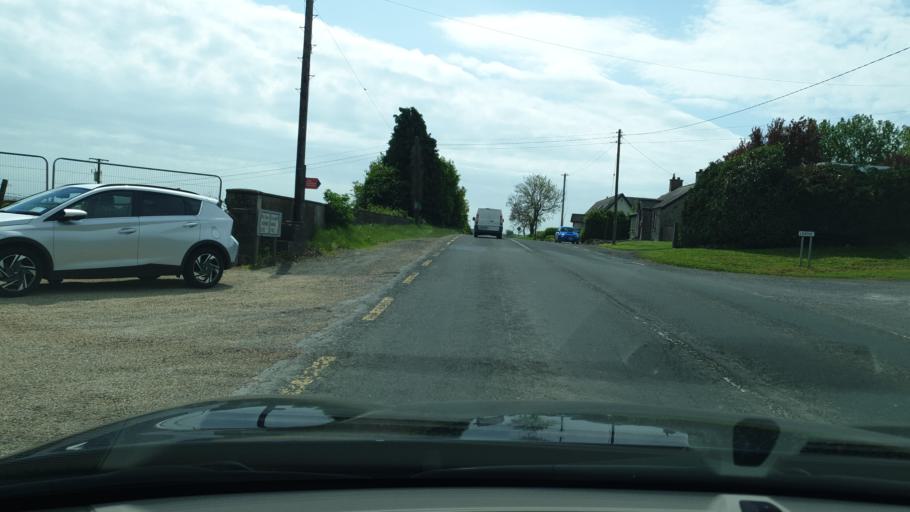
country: IE
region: Ulster
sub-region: An Cabhan
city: Kingscourt
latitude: 53.7917
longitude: -6.7372
